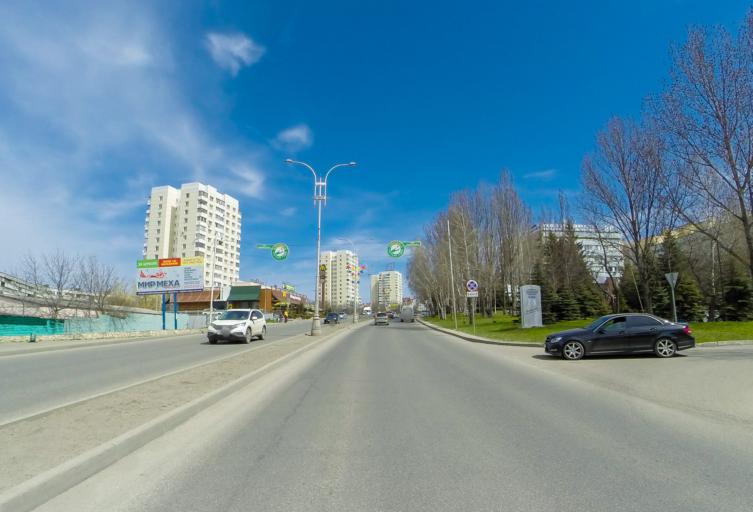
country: RU
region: Stavropol'skiy
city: Pyatigorsk
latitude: 44.0548
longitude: 43.0658
